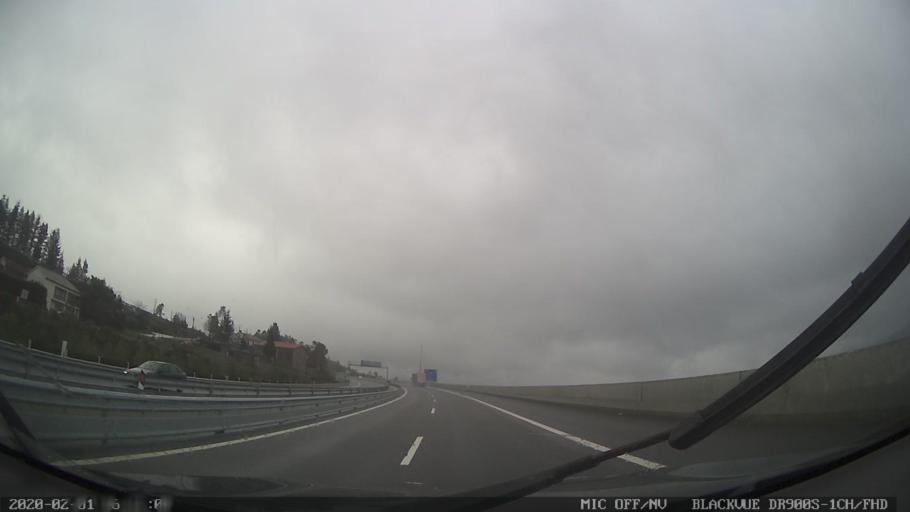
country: PT
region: Vila Real
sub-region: Santa Marta de Penaguiao
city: Santa Marta de Penaguiao
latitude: 41.2764
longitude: -7.8592
